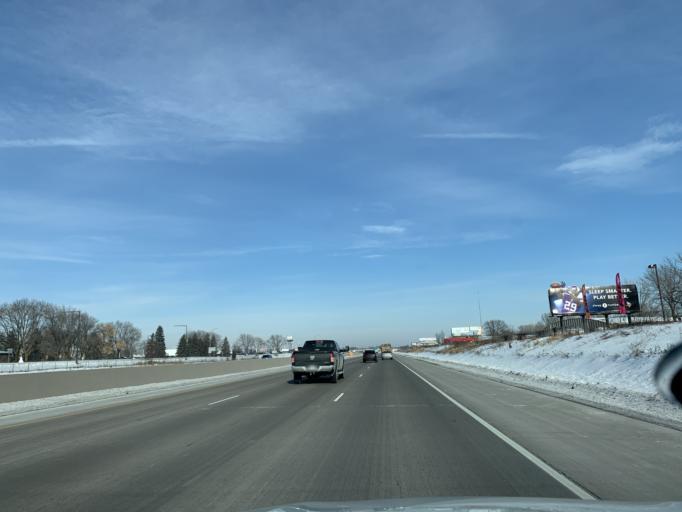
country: US
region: Minnesota
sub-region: Washington County
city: Forest Lake
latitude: 45.2694
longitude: -93.0082
